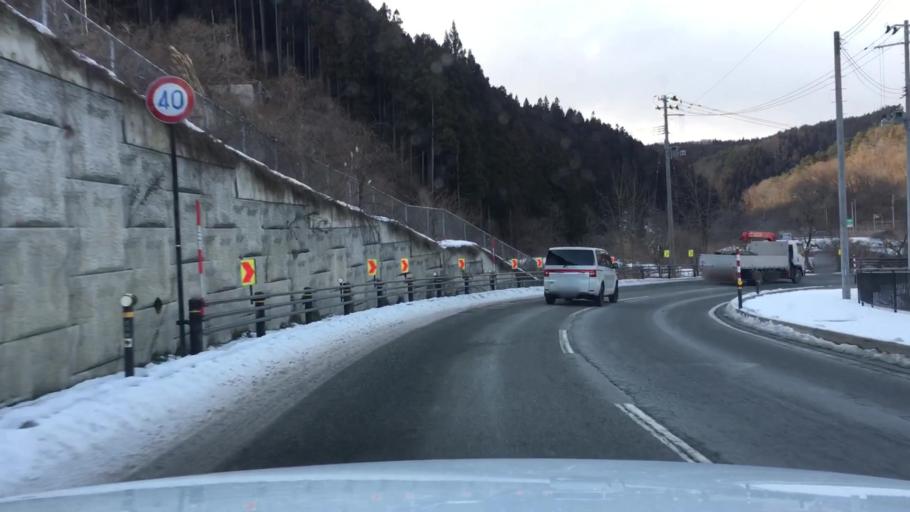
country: JP
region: Iwate
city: Morioka-shi
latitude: 39.6727
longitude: 141.2293
